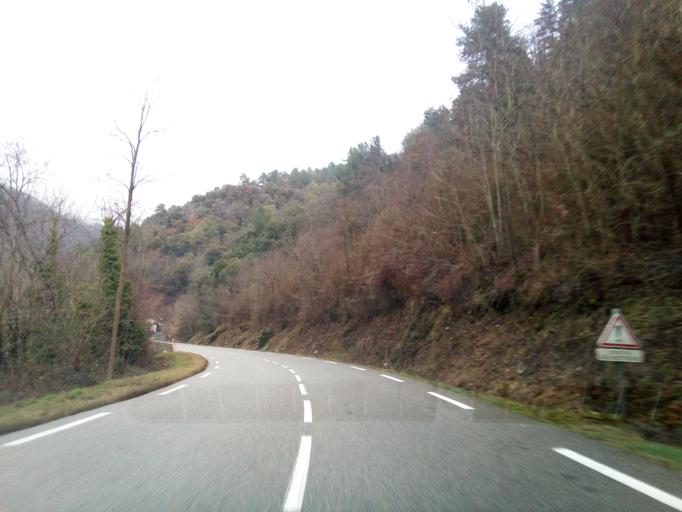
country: FR
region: Rhone-Alpes
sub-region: Departement de l'Ardeche
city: Saint-Sauveur-de-Montagut
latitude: 44.8170
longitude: 4.6042
